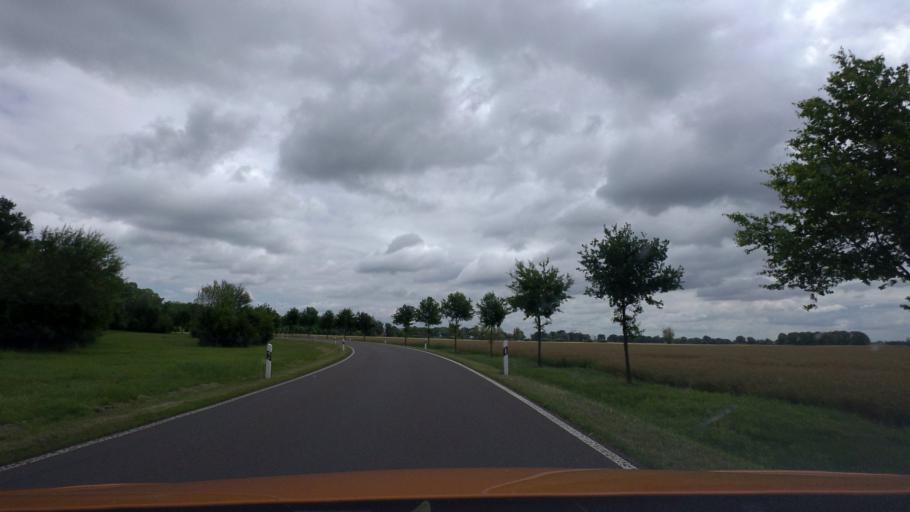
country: DE
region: Brandenburg
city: Bliesdorf
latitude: 52.6740
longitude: 14.1674
